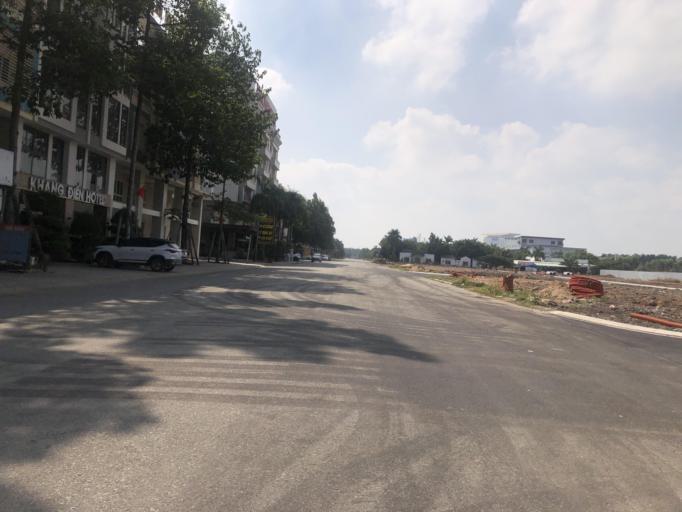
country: VN
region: Binh Duong
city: Thu Dau Mot
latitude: 11.0726
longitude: 106.6827
